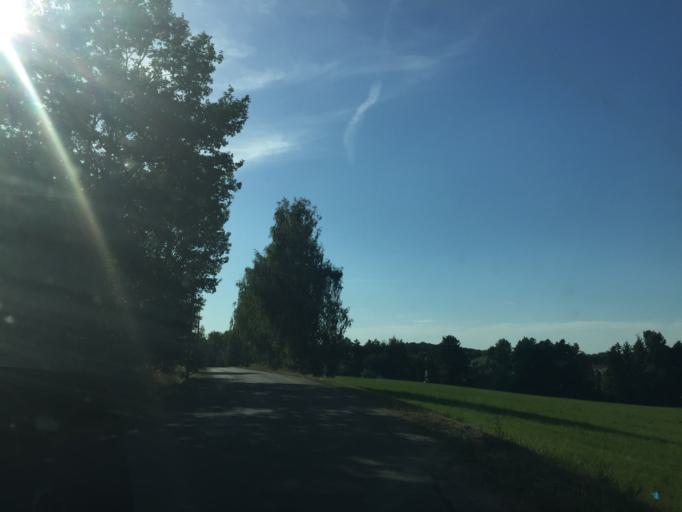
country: DE
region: Thuringia
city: Heyersdorf
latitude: 50.8595
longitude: 12.3348
